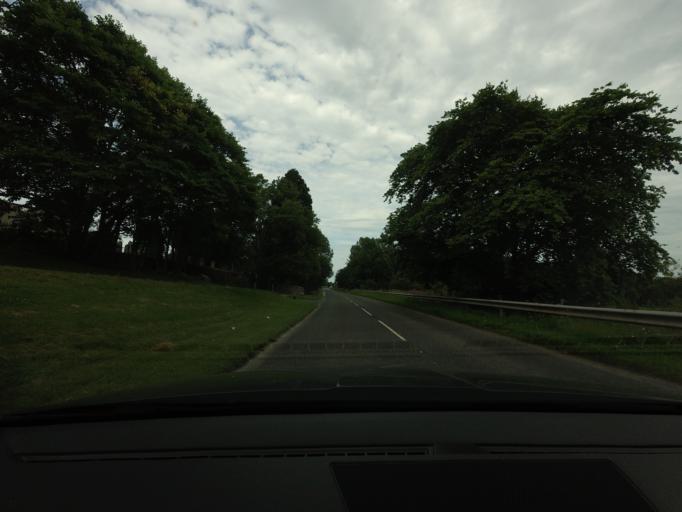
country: GB
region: Scotland
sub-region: Highland
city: Alness
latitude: 57.6906
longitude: -4.2747
